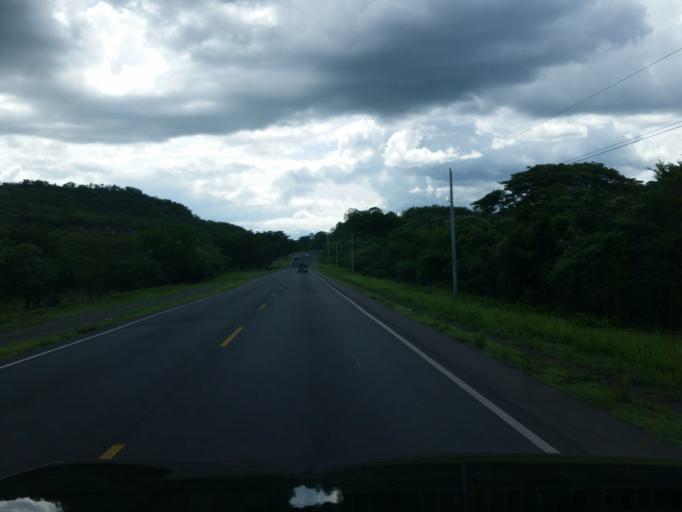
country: NI
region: Managua
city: Valle San Francisco
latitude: 12.4809
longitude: -86.0567
